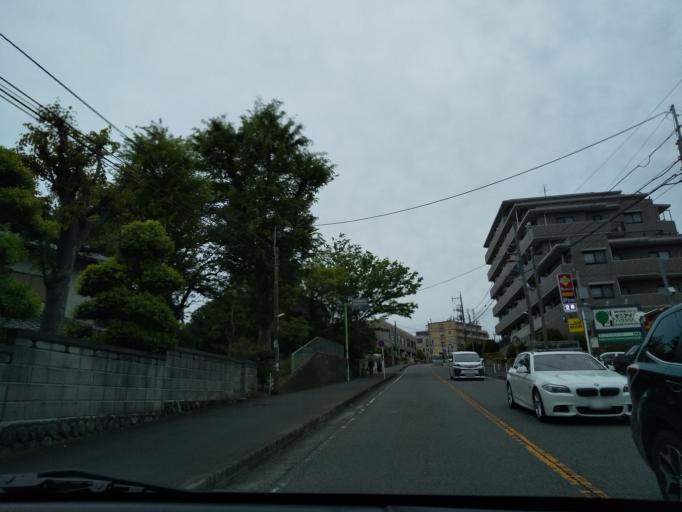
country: JP
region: Tokyo
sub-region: Machida-shi
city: Machida
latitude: 35.5375
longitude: 139.4440
